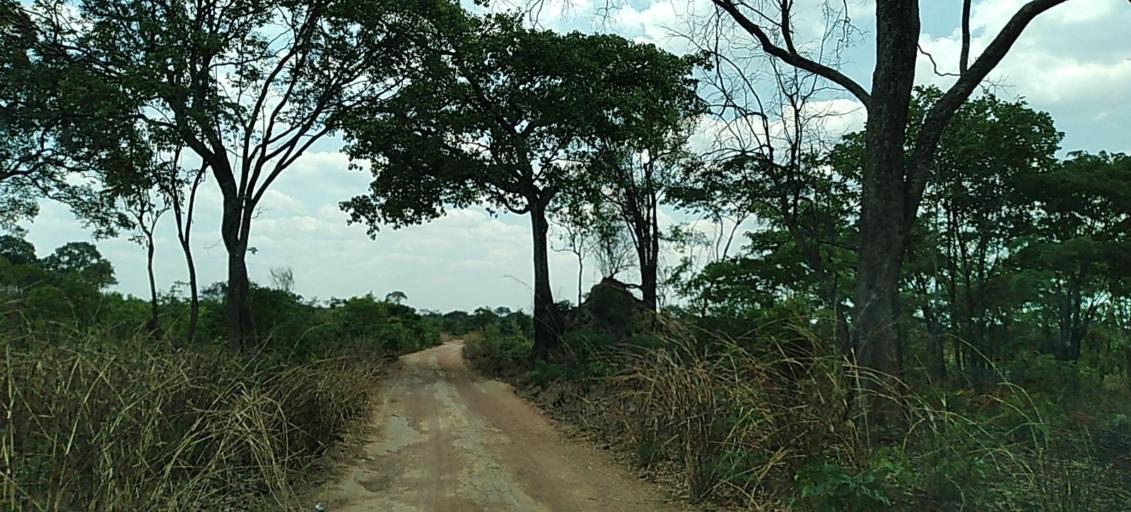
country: ZM
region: Copperbelt
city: Chililabombwe
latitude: -12.3911
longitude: 27.9204
